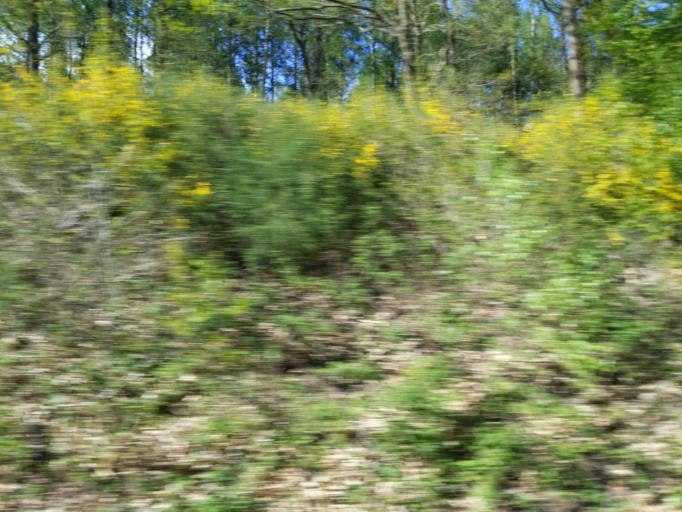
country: DE
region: Saxony
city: Radeberg
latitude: 51.1225
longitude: 13.8684
